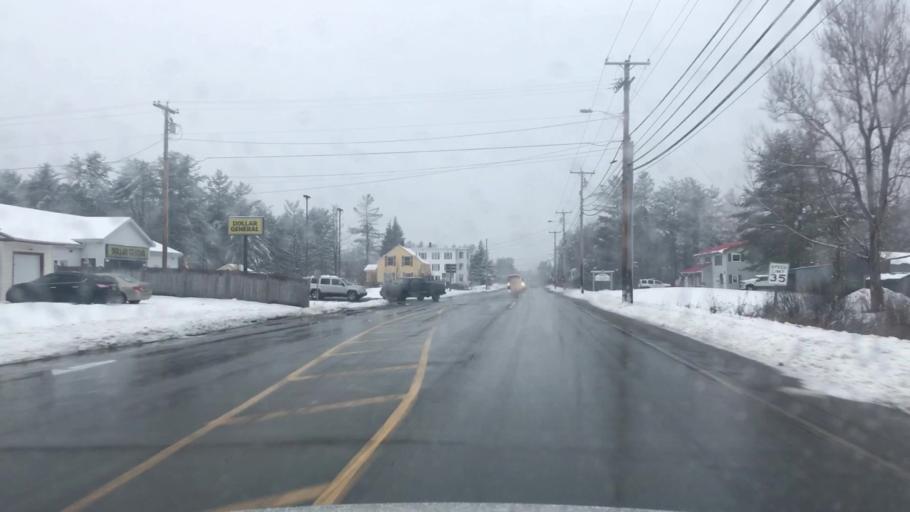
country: US
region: Maine
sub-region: Kennebec County
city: Augusta
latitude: 44.3043
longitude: -69.7436
